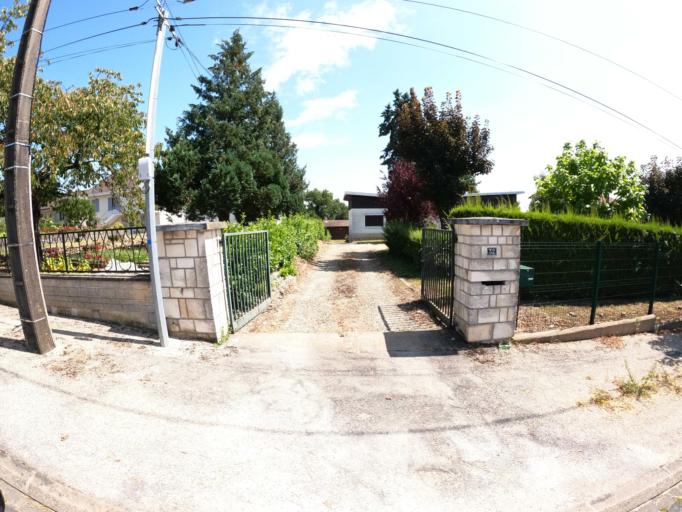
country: FR
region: Poitou-Charentes
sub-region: Departement de la Vienne
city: Civray
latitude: 46.1534
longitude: 0.2965
